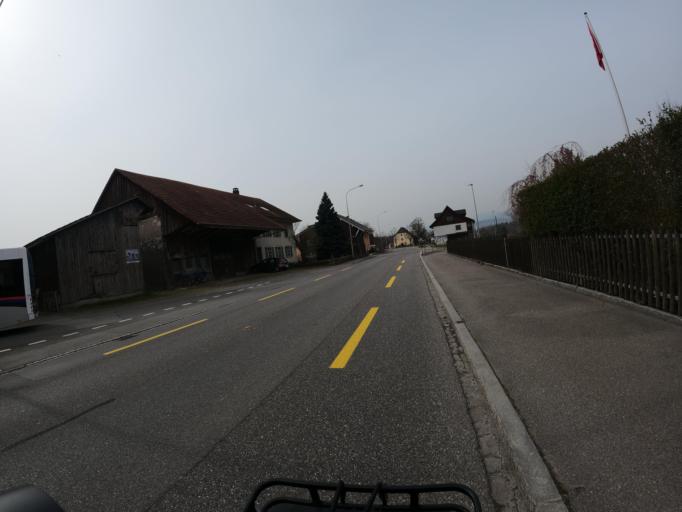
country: CH
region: Aargau
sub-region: Bezirk Aarau
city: Biberstein
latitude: 47.4046
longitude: 8.0880
